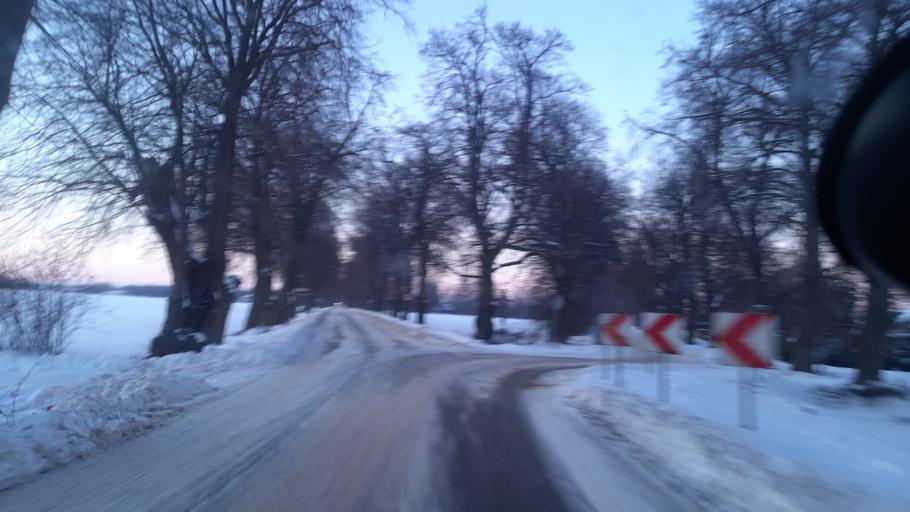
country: PL
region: Lublin Voivodeship
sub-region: Powiat lubelski
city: Lublin
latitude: 51.3251
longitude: 22.5605
